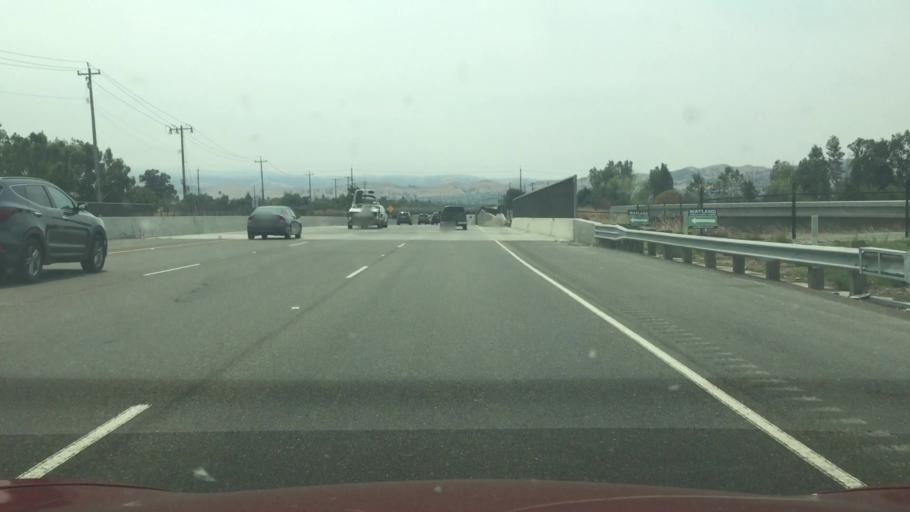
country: US
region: California
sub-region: Alameda County
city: Livermore
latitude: 37.6803
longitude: -121.8055
